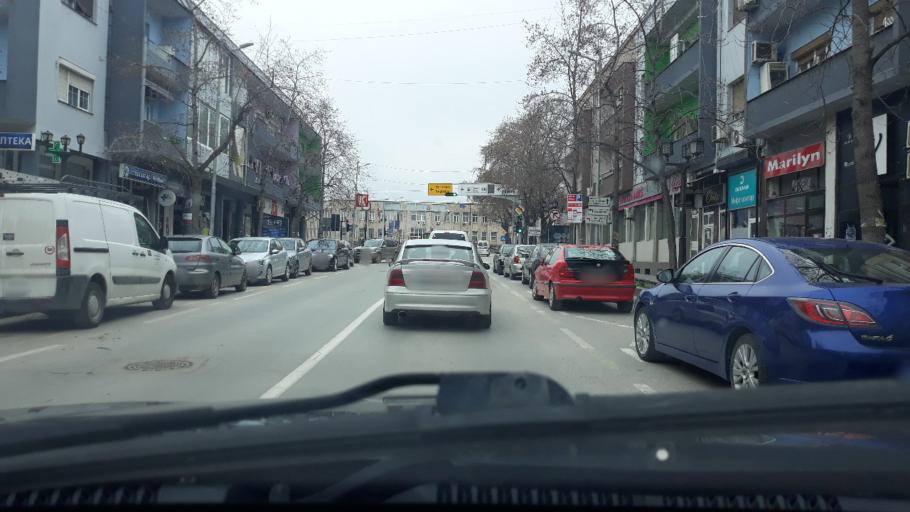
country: MK
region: Kavadarci
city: Kavadarci
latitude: 41.4343
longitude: 22.0116
